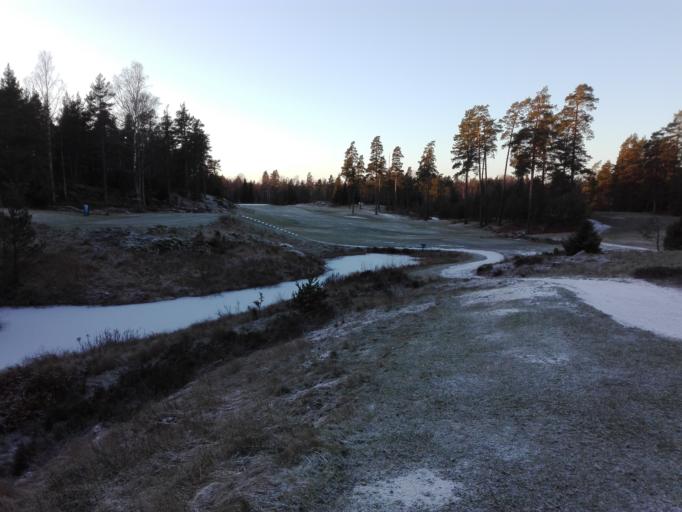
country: SE
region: Stockholm
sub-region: Nacka Kommun
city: Fisksatra
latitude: 59.2850
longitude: 18.2422
